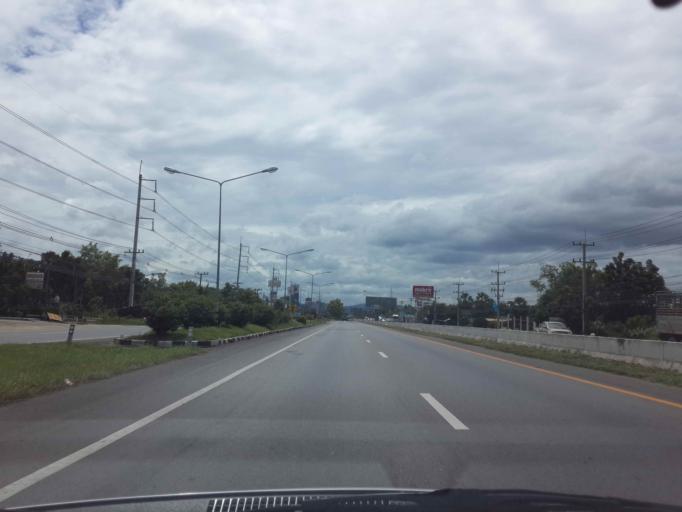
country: TH
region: Phetchaburi
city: Phetchaburi
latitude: 13.1220
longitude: 99.8909
